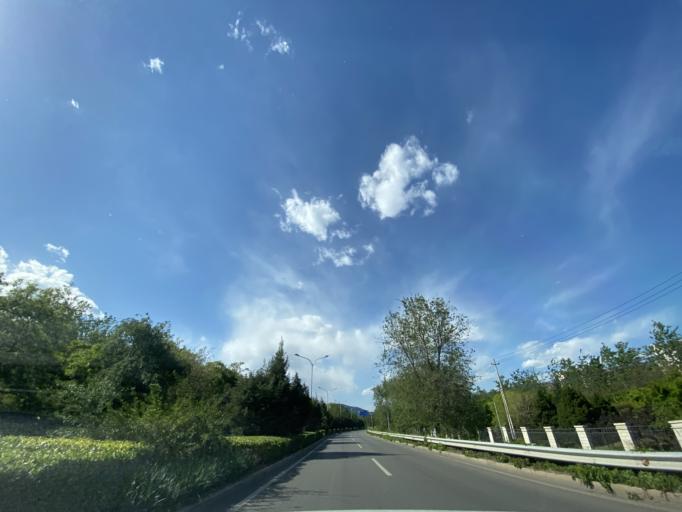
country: CN
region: Beijing
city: Sijiqing
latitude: 39.9637
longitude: 116.2367
